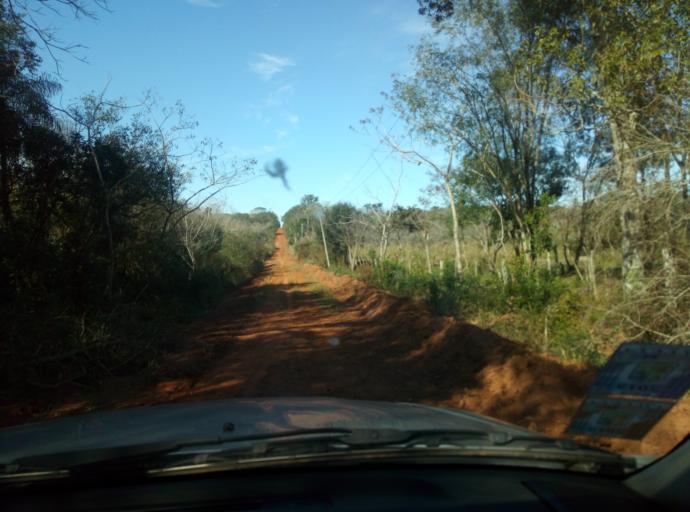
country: PY
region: Caaguazu
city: Carayao
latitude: -25.1697
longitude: -56.3025
